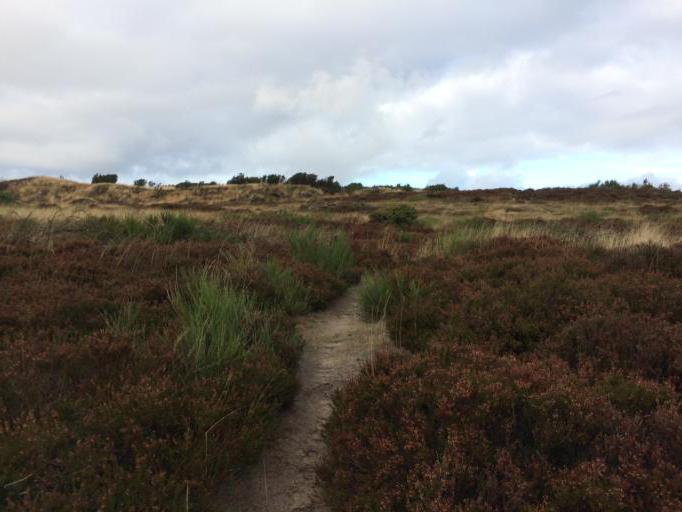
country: DK
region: Central Jutland
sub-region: Holstebro Kommune
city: Ulfborg
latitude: 56.2571
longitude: 8.4092
